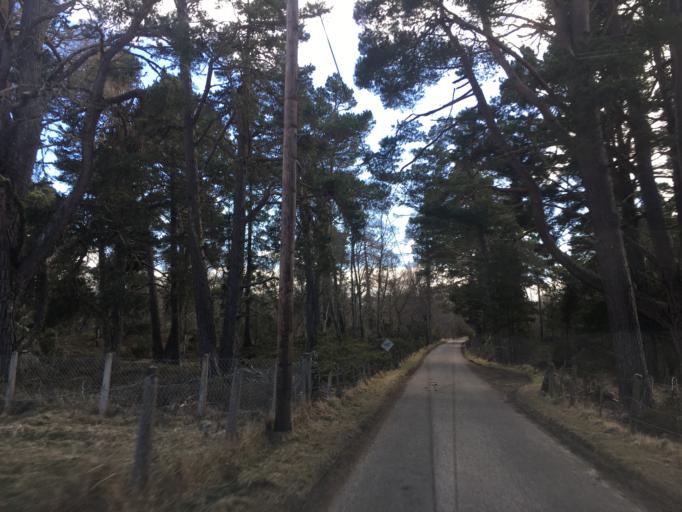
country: GB
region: Scotland
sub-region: Highland
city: Aviemore
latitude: 57.1696
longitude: -3.8111
